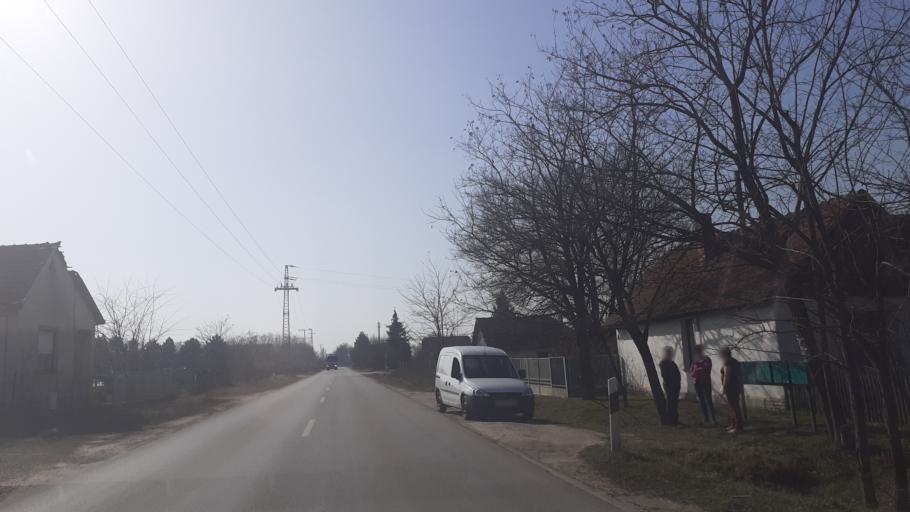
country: HU
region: Bacs-Kiskun
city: Lajosmizse
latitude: 47.0250
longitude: 19.5302
